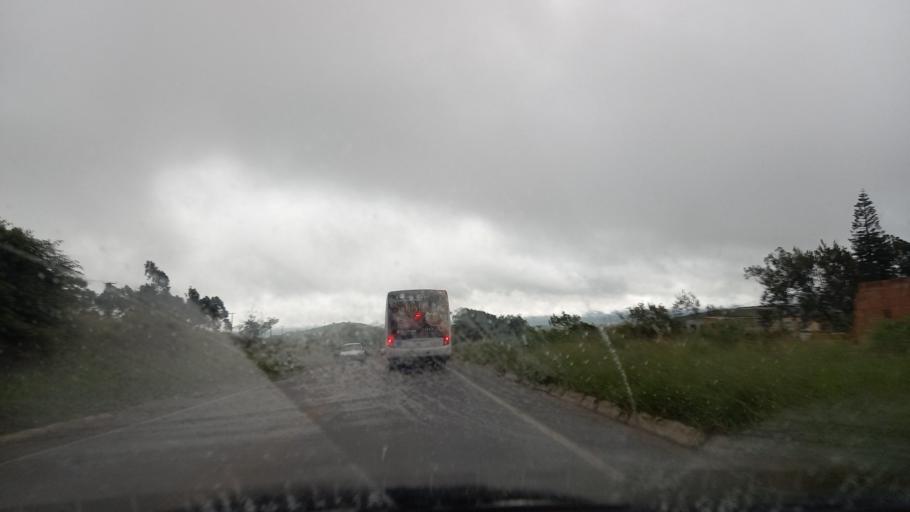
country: BR
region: Pernambuco
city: Garanhuns
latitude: -8.8716
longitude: -36.5079
